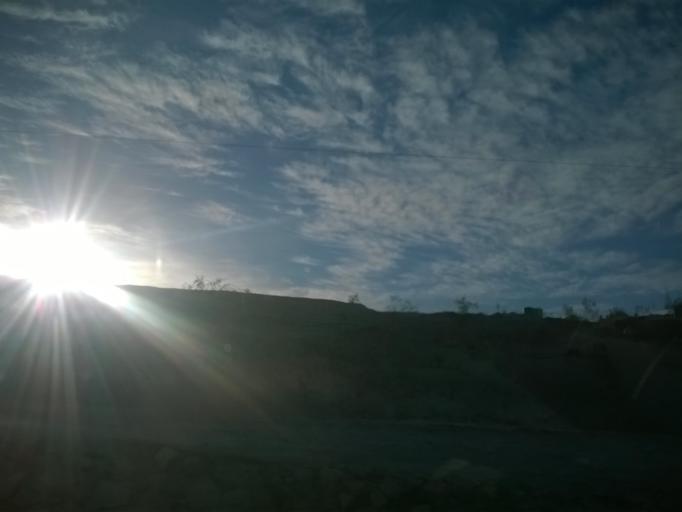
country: LS
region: Berea
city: Teyateyaneng
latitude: -29.1463
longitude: 27.6980
